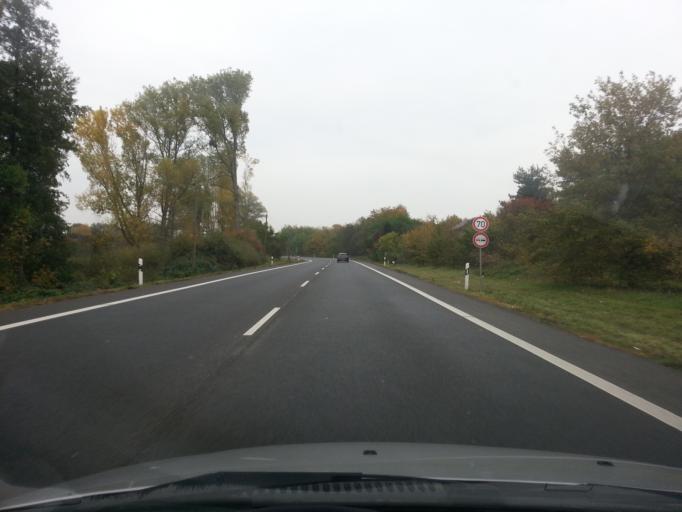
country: DE
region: Hesse
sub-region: Regierungsbezirk Darmstadt
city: Muehlheim am Main
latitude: 50.1225
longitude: 8.8733
